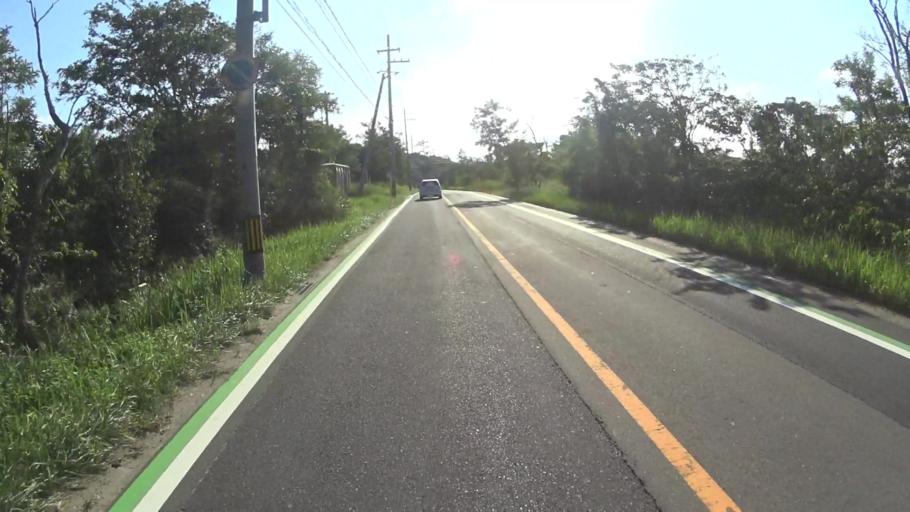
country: JP
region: Hyogo
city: Toyooka
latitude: 35.6578
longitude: 134.9613
